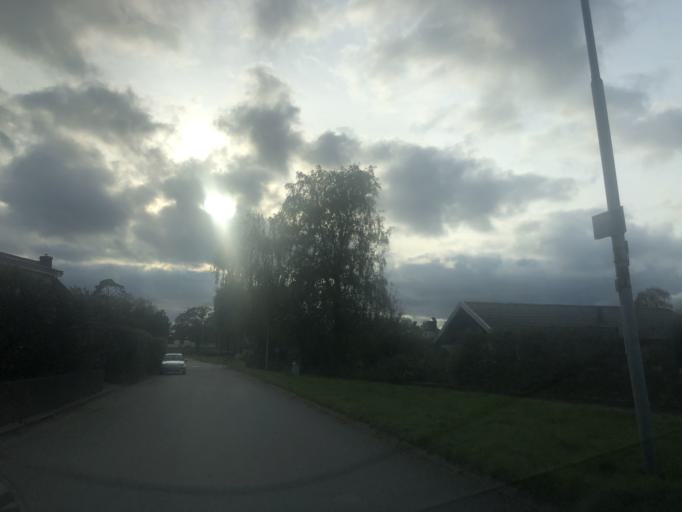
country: SE
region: Vaestra Goetaland
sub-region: Molndal
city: Moelndal
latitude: 57.6343
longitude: 11.9508
